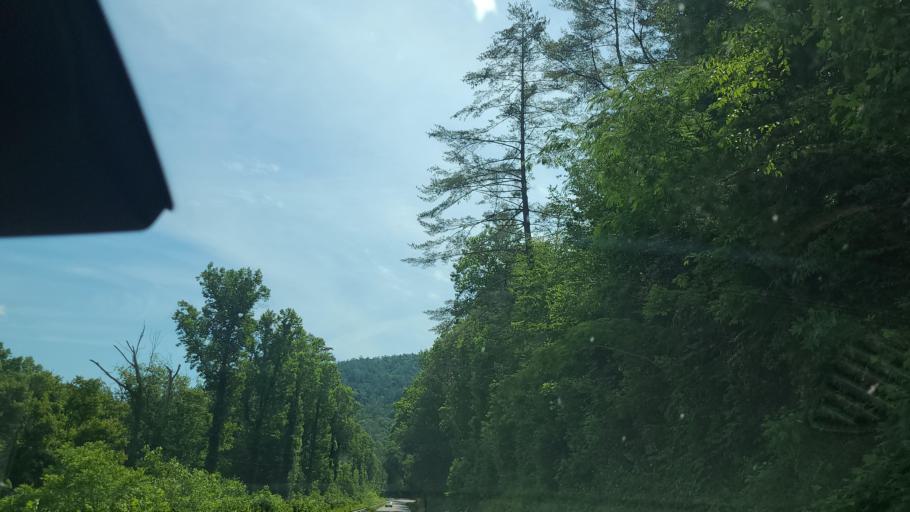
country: US
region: South Carolina
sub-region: Oconee County
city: Walhalla
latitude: 34.9094
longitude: -83.1789
